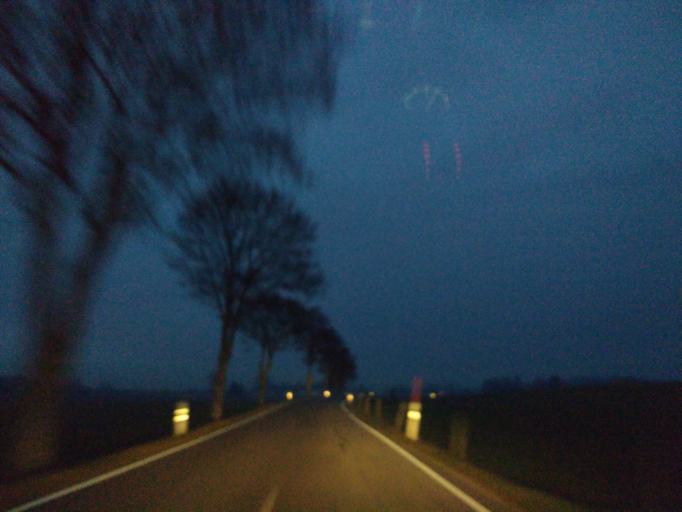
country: DE
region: Bavaria
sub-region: Swabia
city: Stottwang
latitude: 47.8741
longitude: 10.6947
